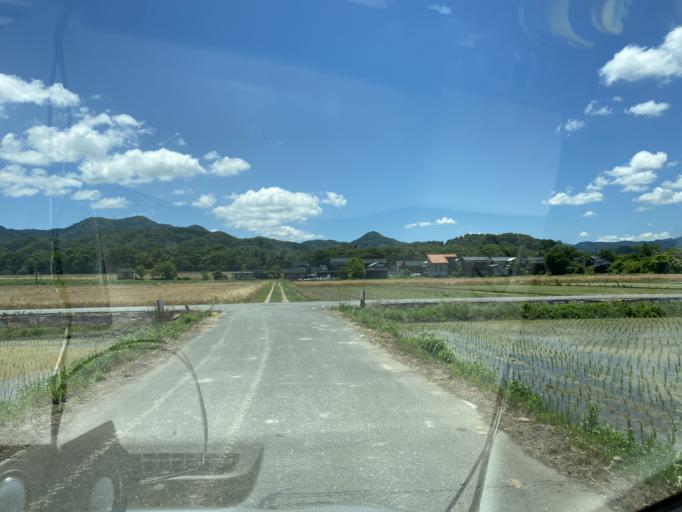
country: JP
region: Hyogo
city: Toyooka
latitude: 35.4845
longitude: 134.7947
